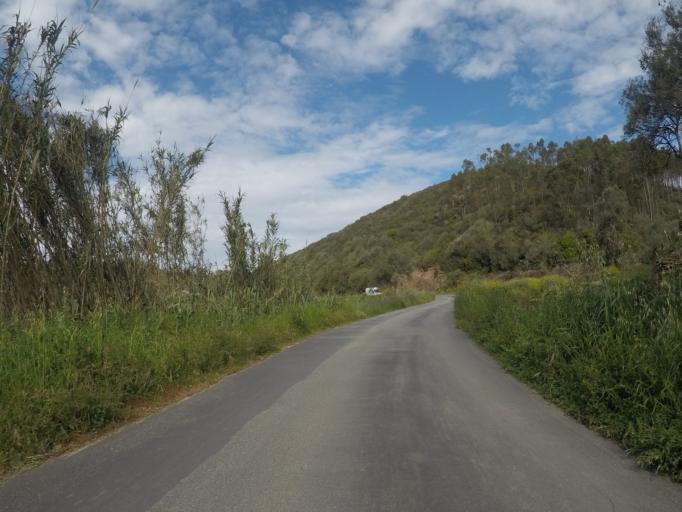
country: PT
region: Beja
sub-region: Odemira
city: Sao Teotonio
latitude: 37.4364
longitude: -8.7844
